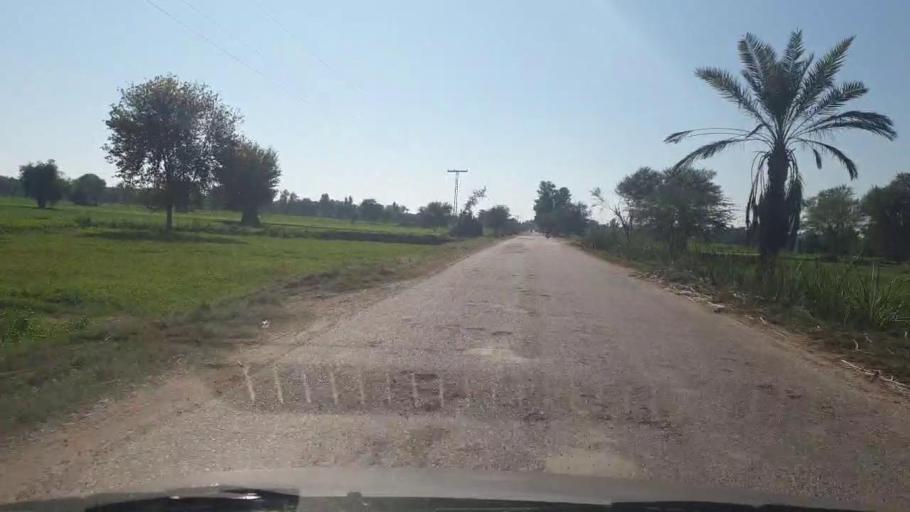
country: PK
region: Sindh
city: Bozdar
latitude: 27.1115
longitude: 68.6340
